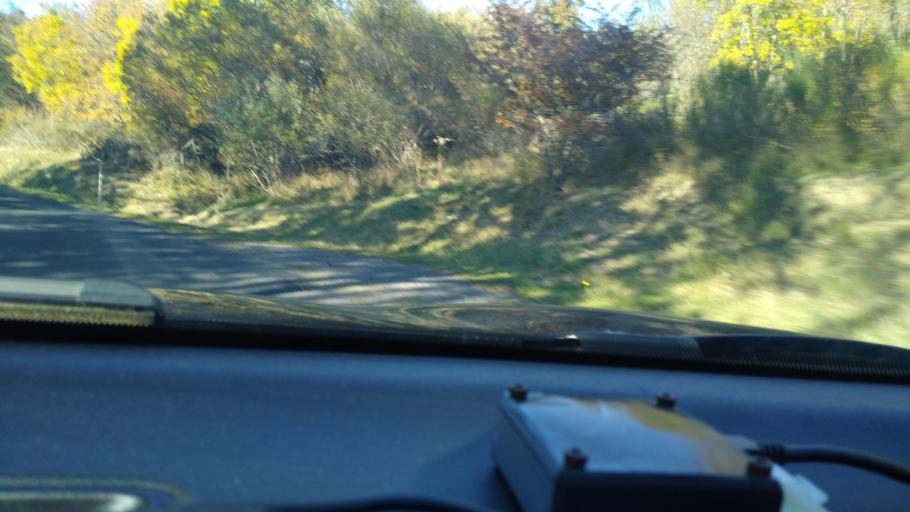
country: FR
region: Languedoc-Roussillon
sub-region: Departement de l'Aude
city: Quillan
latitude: 42.7277
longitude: 2.1192
